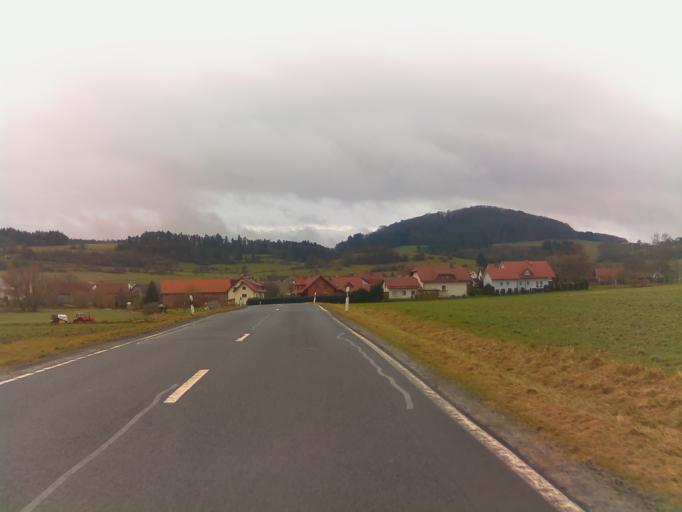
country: DE
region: Hesse
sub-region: Regierungsbezirk Kassel
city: Rasdorf
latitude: 50.6636
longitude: 9.9164
